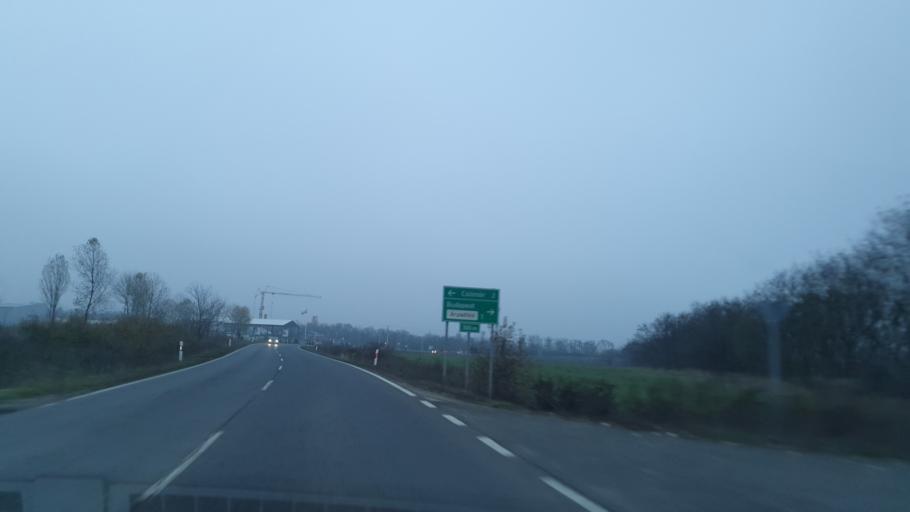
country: HU
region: Pest
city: Csomor
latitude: 47.5434
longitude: 19.2083
